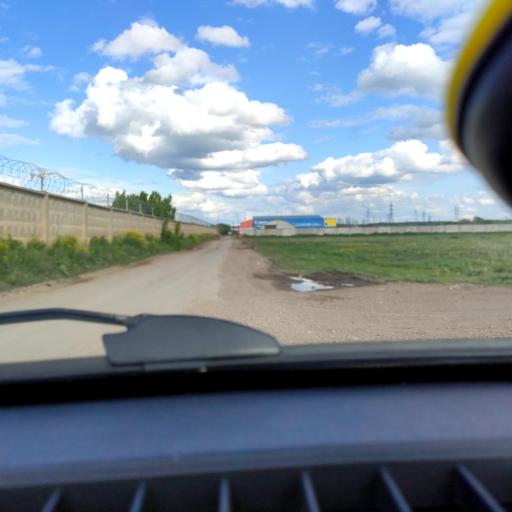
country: RU
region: Samara
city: Tol'yatti
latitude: 53.5463
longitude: 49.4741
